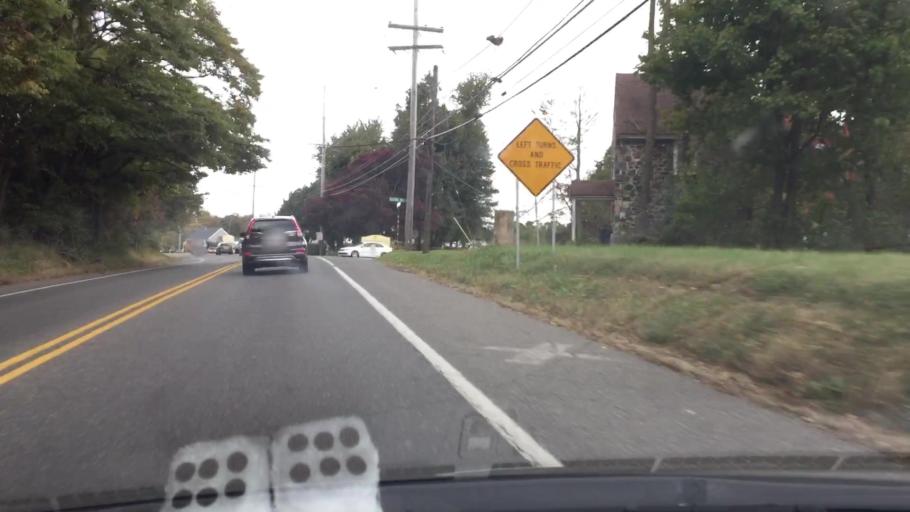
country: US
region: Pennsylvania
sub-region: Delaware County
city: Chester Heights
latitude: 39.9463
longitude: -75.5039
